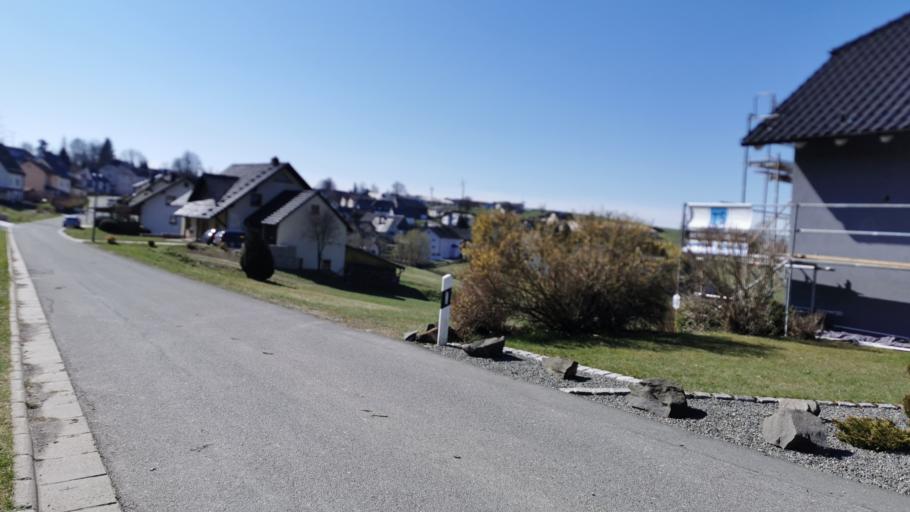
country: DE
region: Bavaria
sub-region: Upper Franconia
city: Teuschnitz
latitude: 50.4177
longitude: 11.3347
